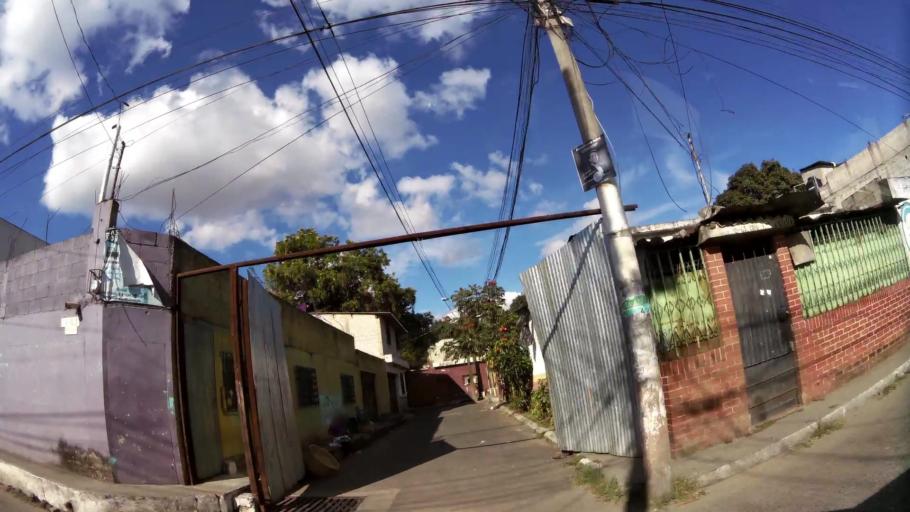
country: GT
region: Guatemala
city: Villa Nueva
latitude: 14.5245
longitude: -90.5824
